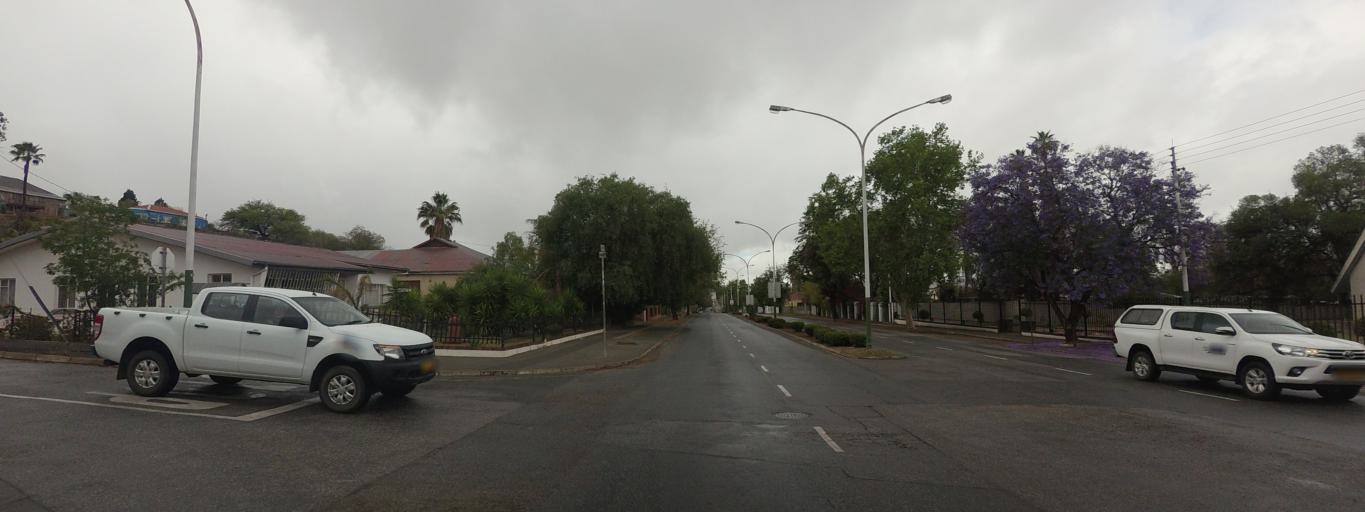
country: ZA
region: Western Cape
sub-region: Eden District Municipality
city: Oudtshoorn
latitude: -33.6031
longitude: 22.2089
